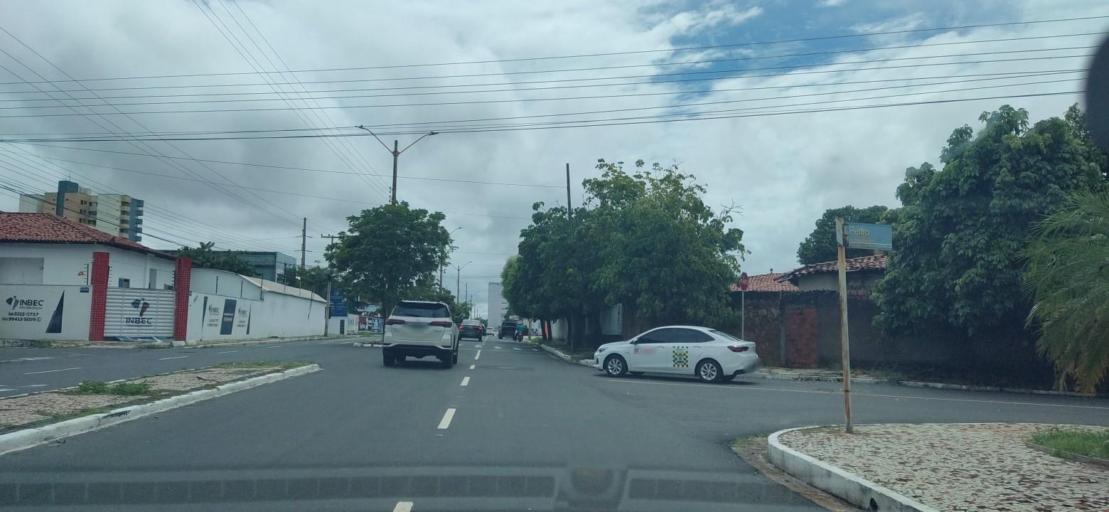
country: BR
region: Piaui
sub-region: Teresina
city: Teresina
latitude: -5.0727
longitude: -42.7761
